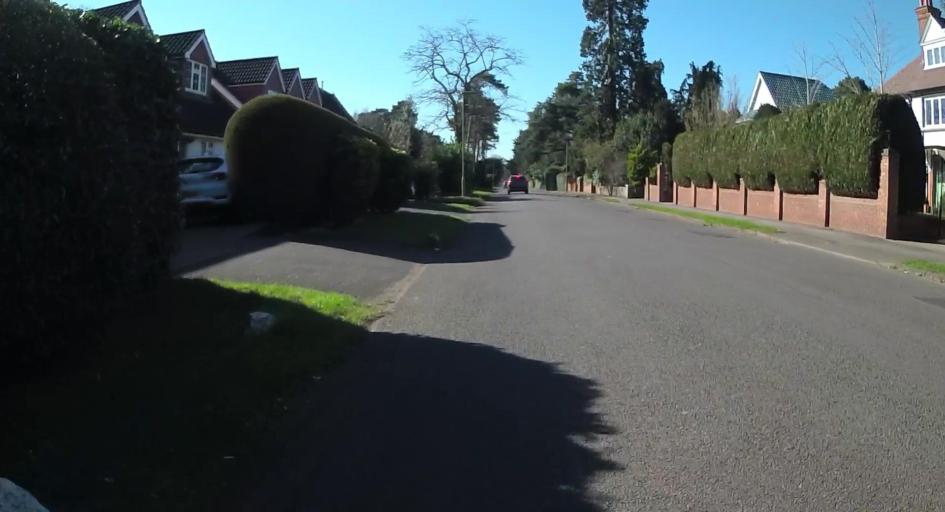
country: GB
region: England
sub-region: Surrey
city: Weybridge
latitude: 51.3694
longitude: -0.4332
